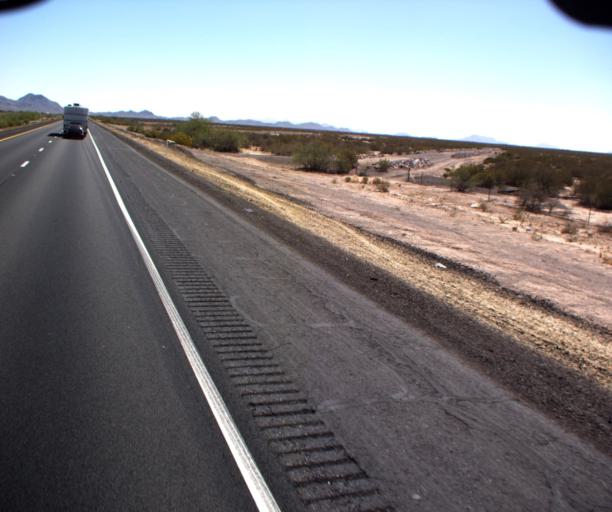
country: US
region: Arizona
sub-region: La Paz County
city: Salome
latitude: 33.6247
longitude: -113.7270
